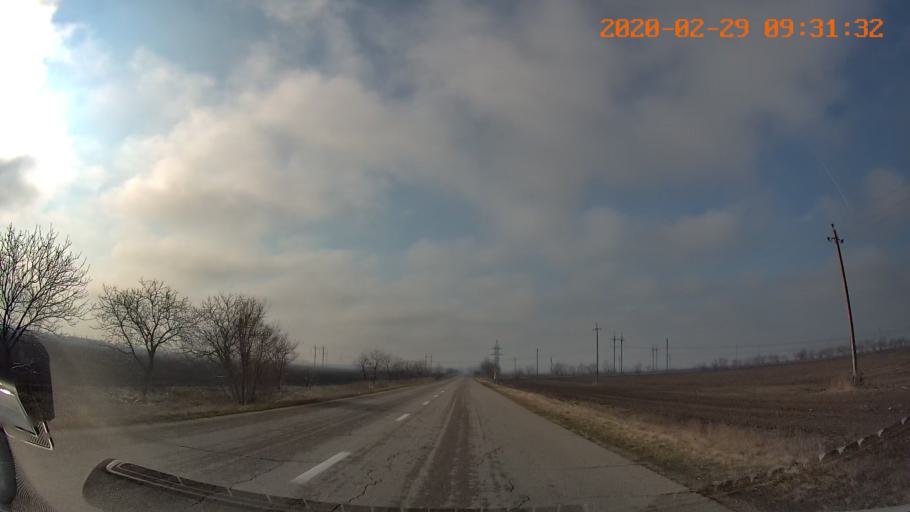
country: MD
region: Telenesti
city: Dnestrovsc
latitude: 46.6517
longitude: 29.9108
